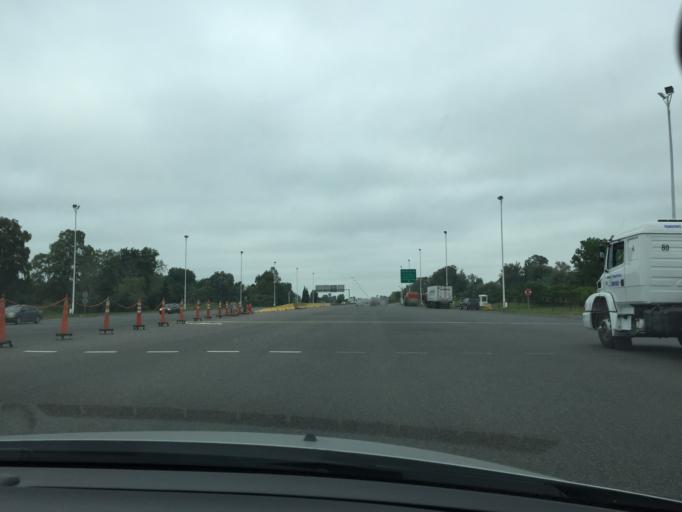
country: AR
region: Buenos Aires
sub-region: Partido de Ezeiza
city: Ezeiza
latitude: -34.8543
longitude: -58.5523
